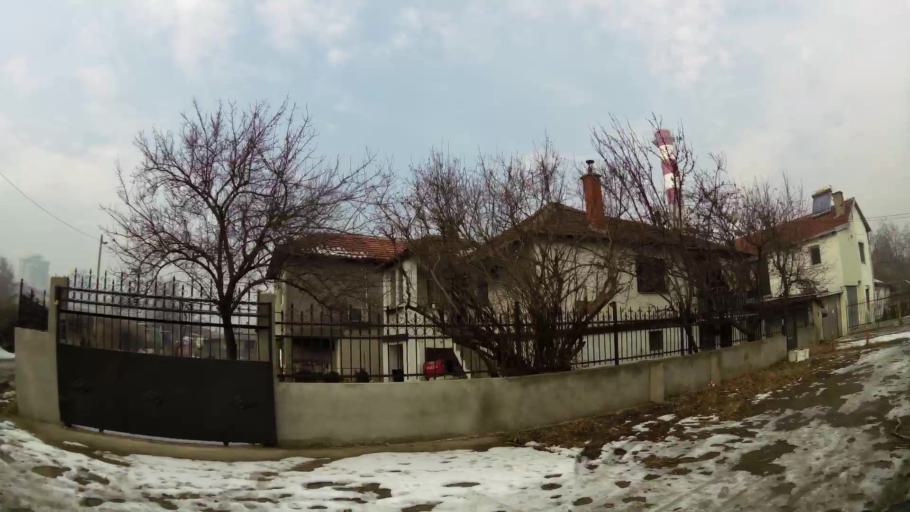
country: MK
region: Karpos
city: Skopje
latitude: 41.9923
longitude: 21.4544
